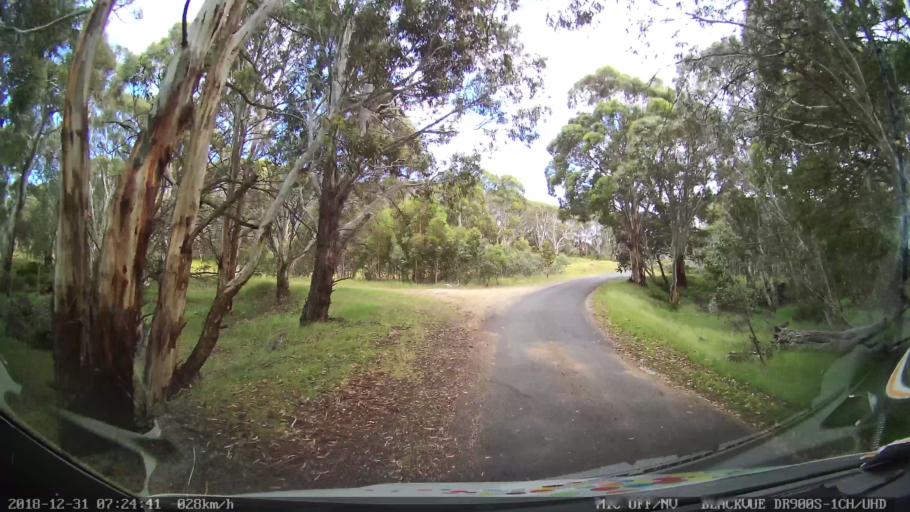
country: AU
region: New South Wales
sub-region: Snowy River
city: Jindabyne
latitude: -36.3228
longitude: 148.4744
